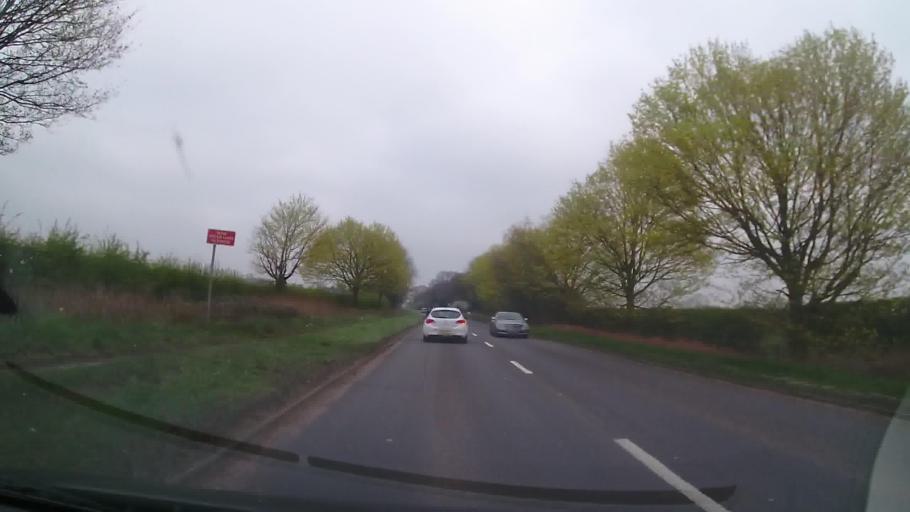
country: GB
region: England
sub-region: Shropshire
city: Market Drayton
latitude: 52.9137
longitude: -2.4508
